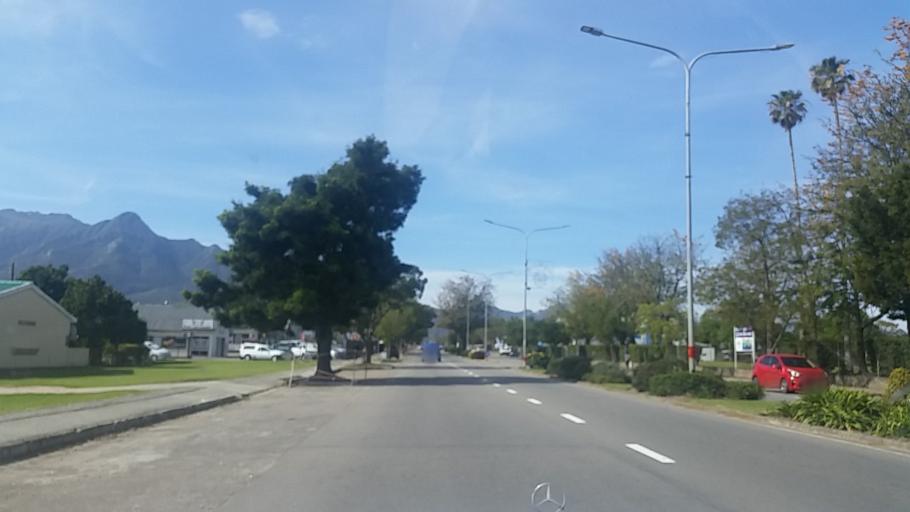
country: ZA
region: Western Cape
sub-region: Eden District Municipality
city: George
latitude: -33.9697
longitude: 22.4481
